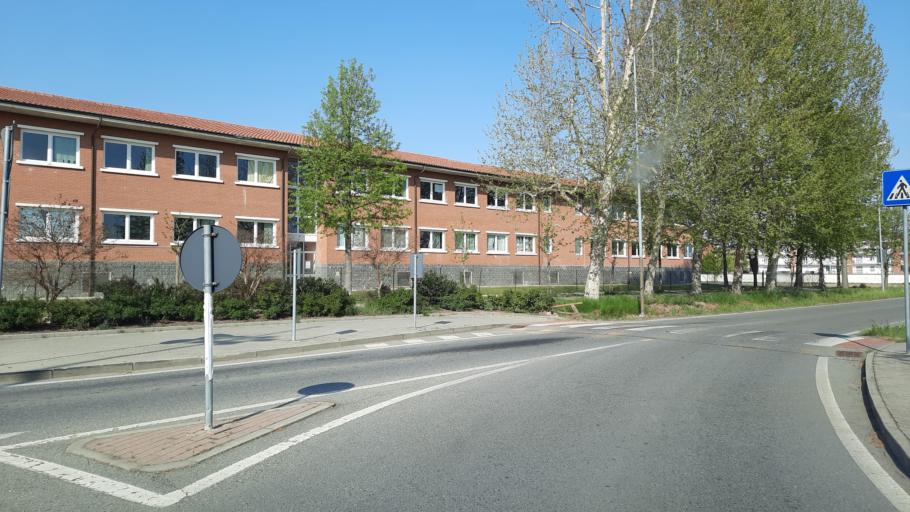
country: IT
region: Piedmont
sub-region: Provincia di Vercelli
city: Crescentino
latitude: 45.1910
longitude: 8.1086
